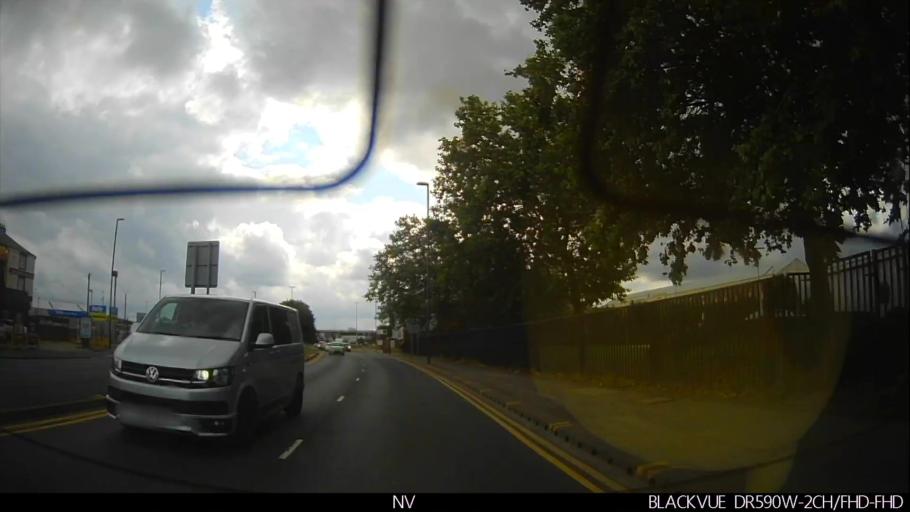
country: GB
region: England
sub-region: City and Borough of Leeds
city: Leeds
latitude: 53.7870
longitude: -1.5345
